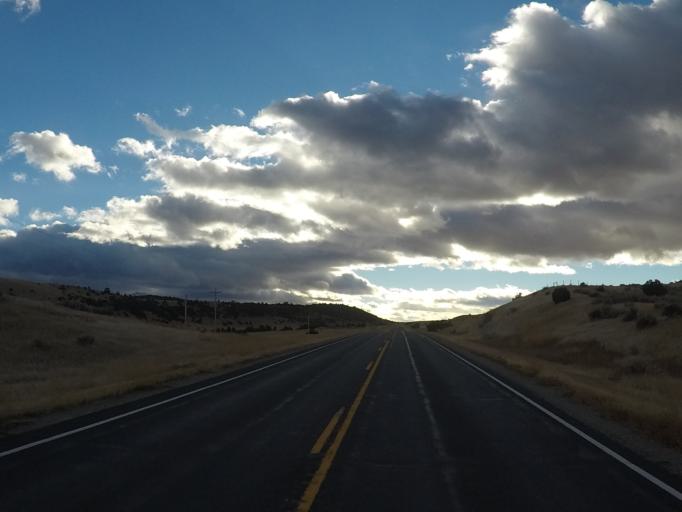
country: US
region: Montana
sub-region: Jefferson County
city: Whitehall
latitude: 45.9109
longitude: -111.9403
